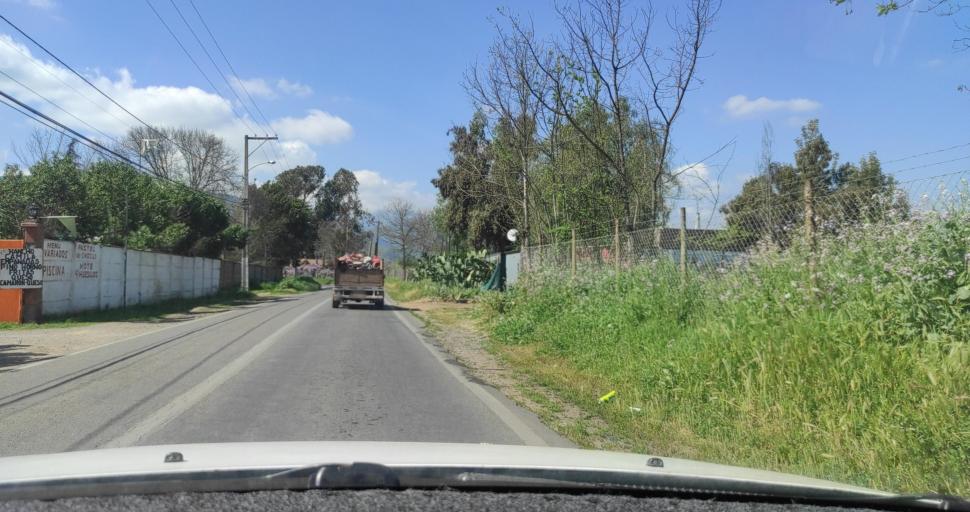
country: CL
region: Valparaiso
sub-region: Provincia de Marga Marga
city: Limache
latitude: -33.0060
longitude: -71.2405
